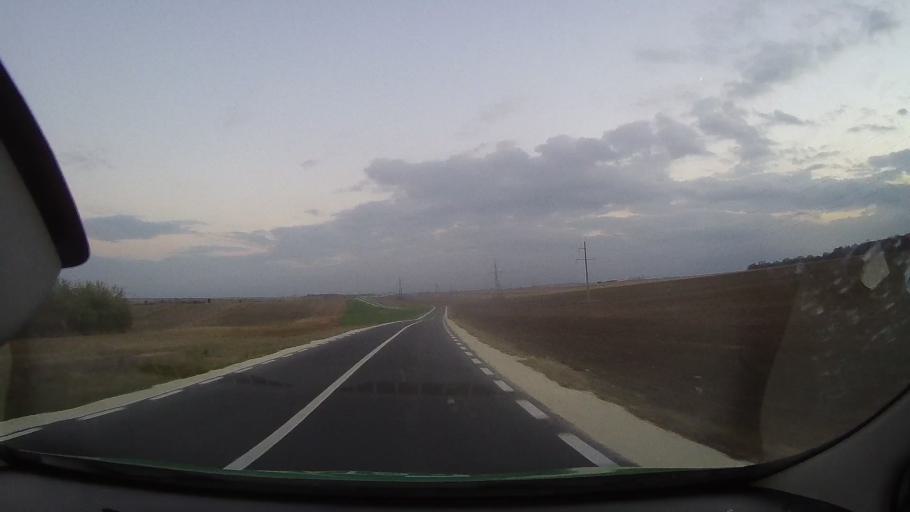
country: RO
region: Constanta
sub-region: Comuna Baneasa
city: Baneasa
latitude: 44.1085
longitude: 27.6702
